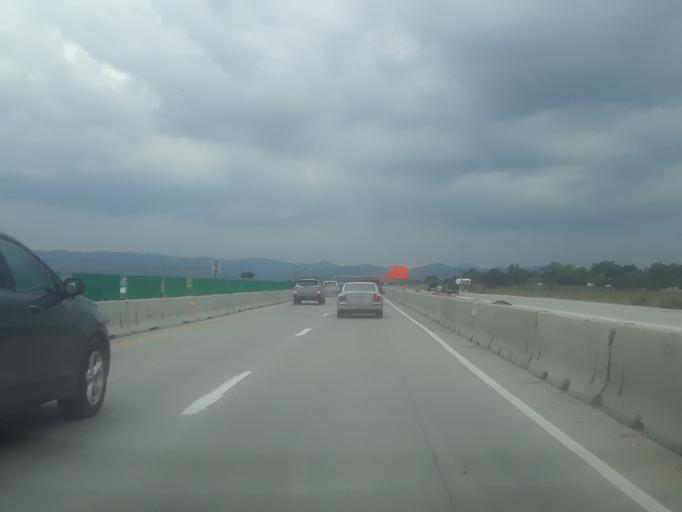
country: US
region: Colorado
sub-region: Jefferson County
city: Columbine
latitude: 39.5665
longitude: -105.0563
